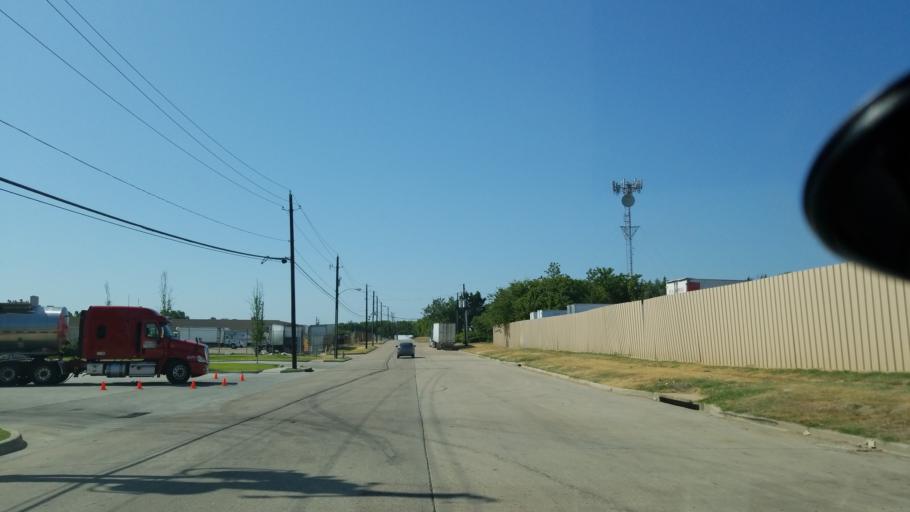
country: US
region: Texas
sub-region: Dallas County
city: Duncanville
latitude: 32.6951
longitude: -96.9161
